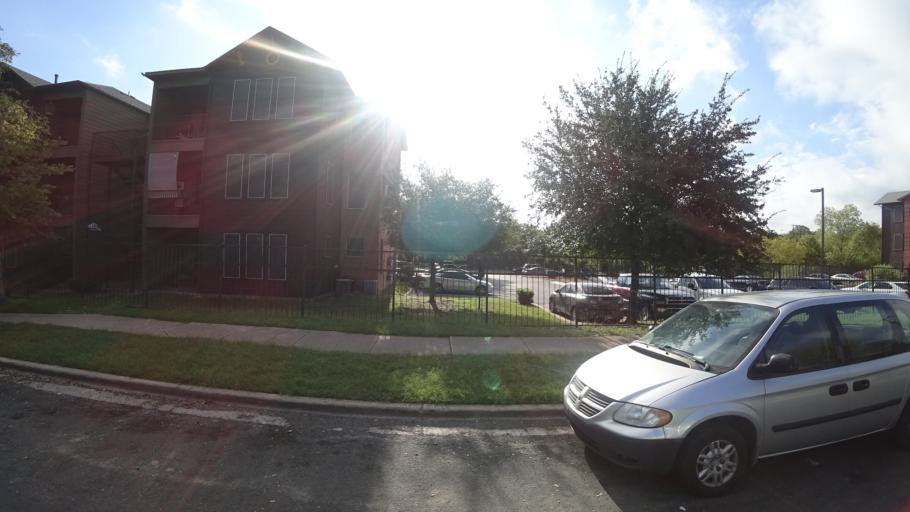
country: US
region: Texas
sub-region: Travis County
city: Austin
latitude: 30.3329
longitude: -97.6924
